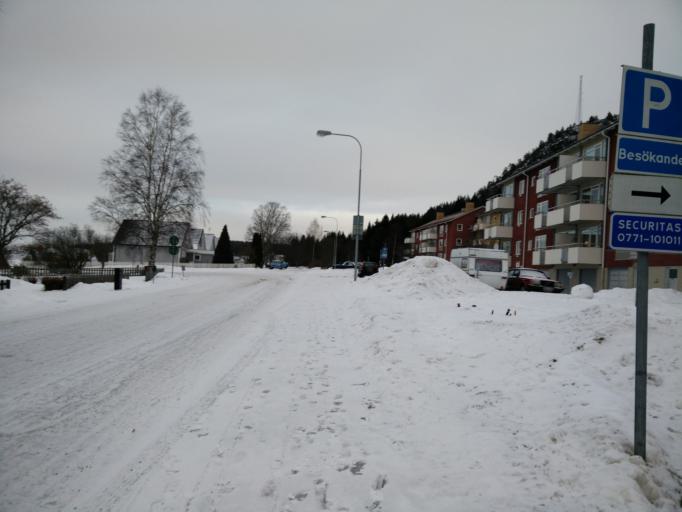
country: SE
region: Vaesternorrland
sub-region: Sundsvalls Kommun
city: Kvissleby
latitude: 62.2954
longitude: 17.3699
